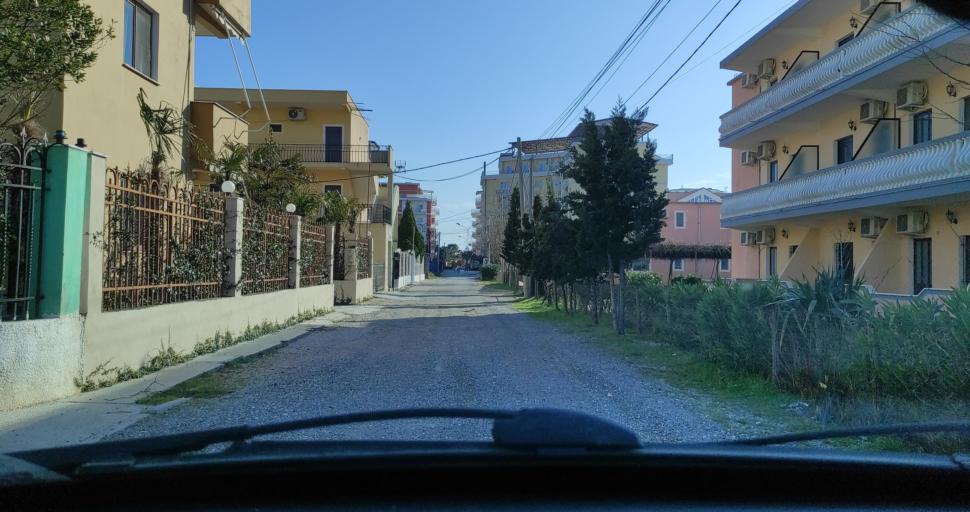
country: AL
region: Shkoder
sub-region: Rrethi i Shkodres
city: Velipoje
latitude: 41.8645
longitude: 19.4301
